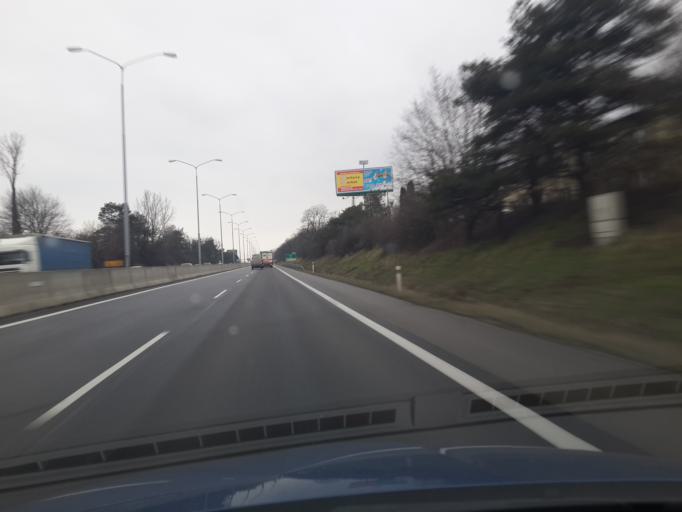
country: AT
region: Lower Austria
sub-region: Politischer Bezirk Bruck an der Leitha
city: Wolfsthal
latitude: 48.1914
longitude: 17.0447
